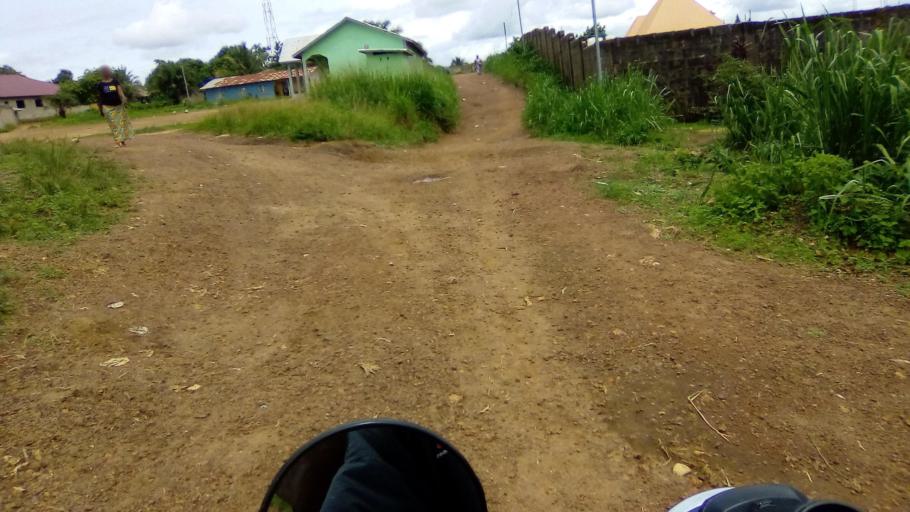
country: SL
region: Southern Province
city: Bo
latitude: 7.9350
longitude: -11.7224
